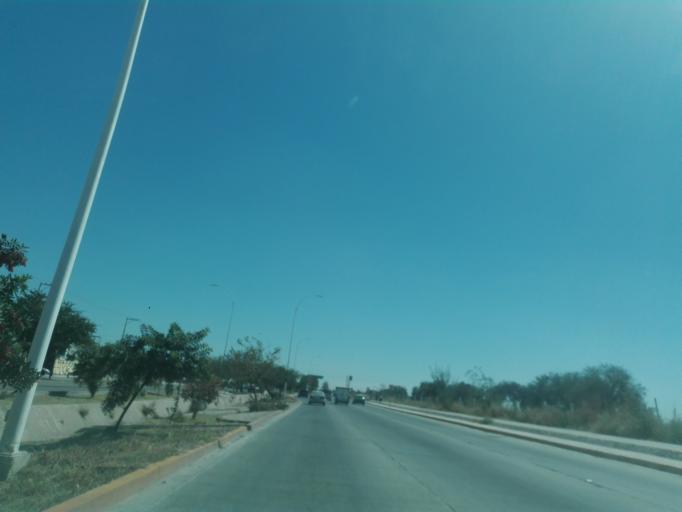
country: MX
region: Guanajuato
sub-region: Leon
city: San Jose de Duran (Los Troncoso)
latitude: 21.0735
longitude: -101.6472
